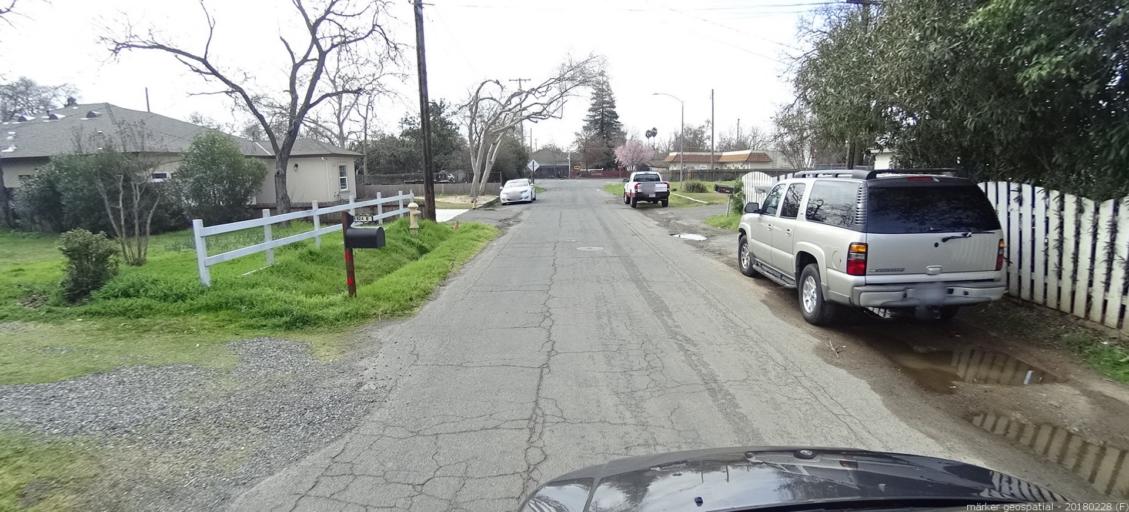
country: US
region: California
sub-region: Sacramento County
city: Rio Linda
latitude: 38.6922
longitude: -121.4465
